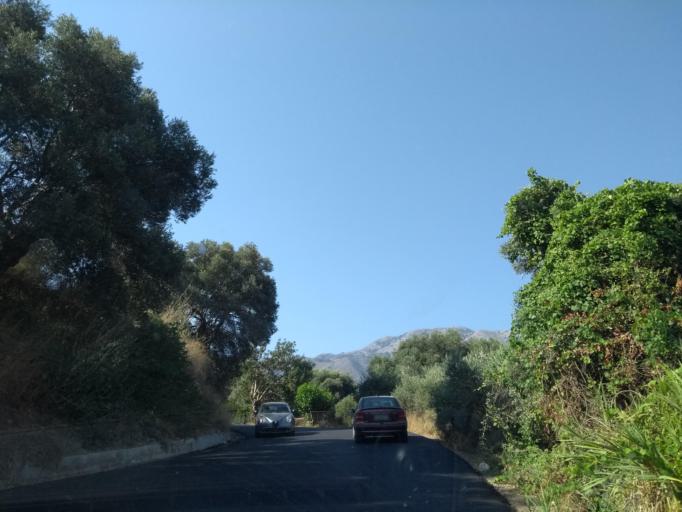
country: GR
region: Crete
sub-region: Nomos Chanias
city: Georgioupolis
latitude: 35.3265
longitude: 24.2998
